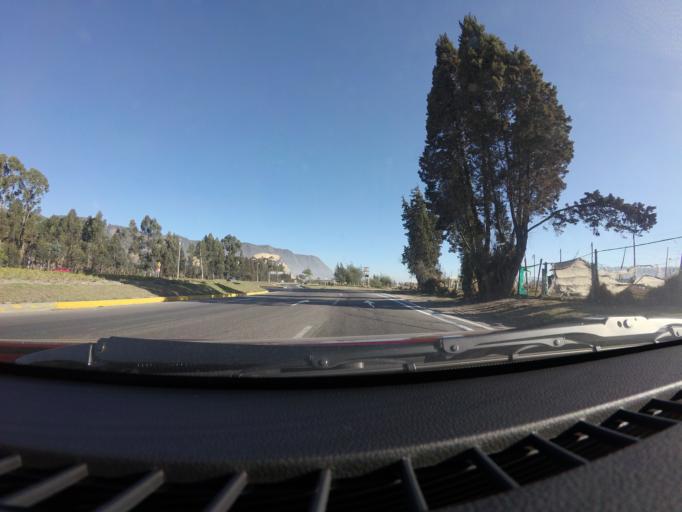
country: CO
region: Cundinamarca
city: Cajica
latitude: 4.9402
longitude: -74.0164
